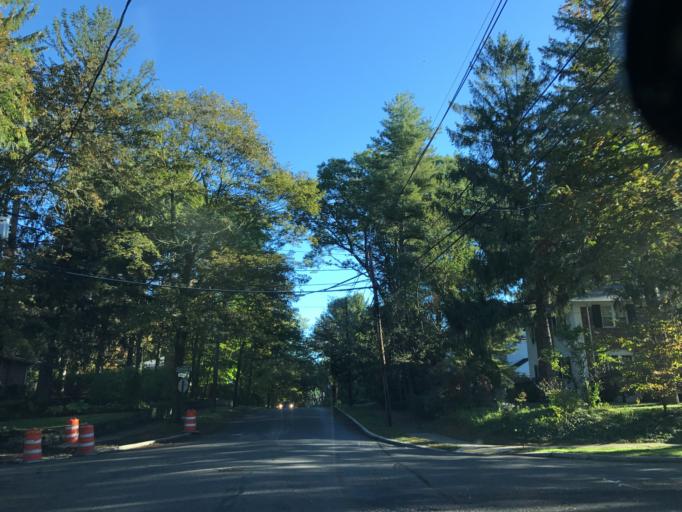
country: US
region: Massachusetts
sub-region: Middlesex County
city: Newton
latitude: 42.3051
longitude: -71.1902
